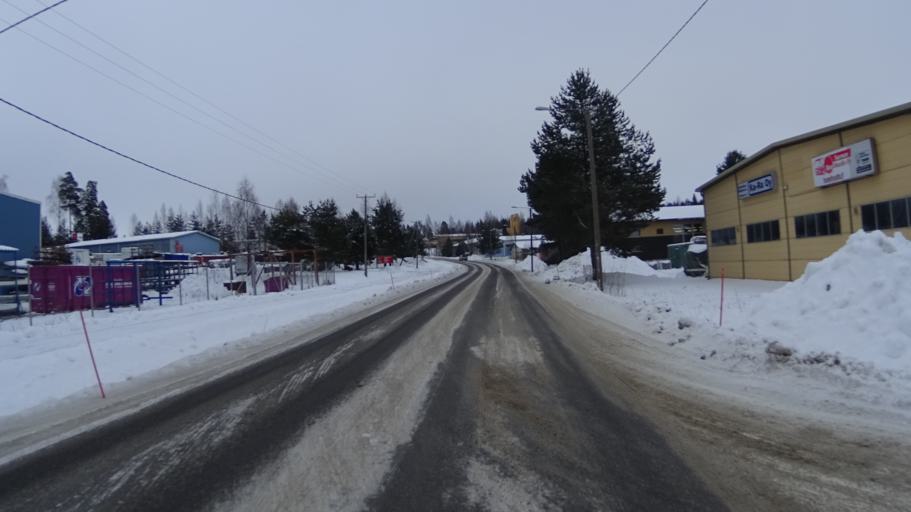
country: FI
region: Uusimaa
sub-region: Helsinki
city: Karkkila
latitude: 60.5206
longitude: 24.2388
